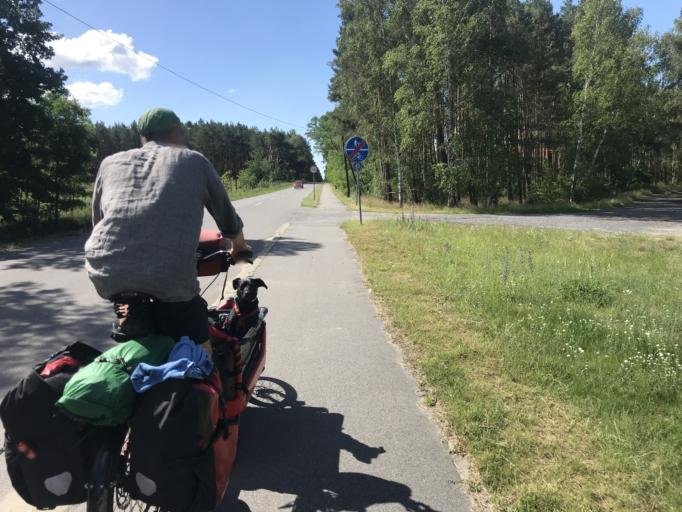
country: PL
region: Lubusz
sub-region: Powiat krosnienski
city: Gubin
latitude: 52.0574
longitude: 14.7625
